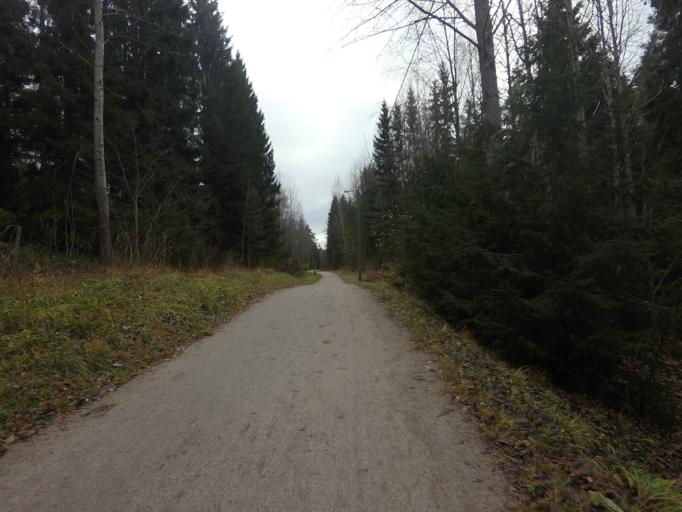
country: FI
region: Uusimaa
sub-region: Helsinki
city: Kauniainen
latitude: 60.1957
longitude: 24.6991
